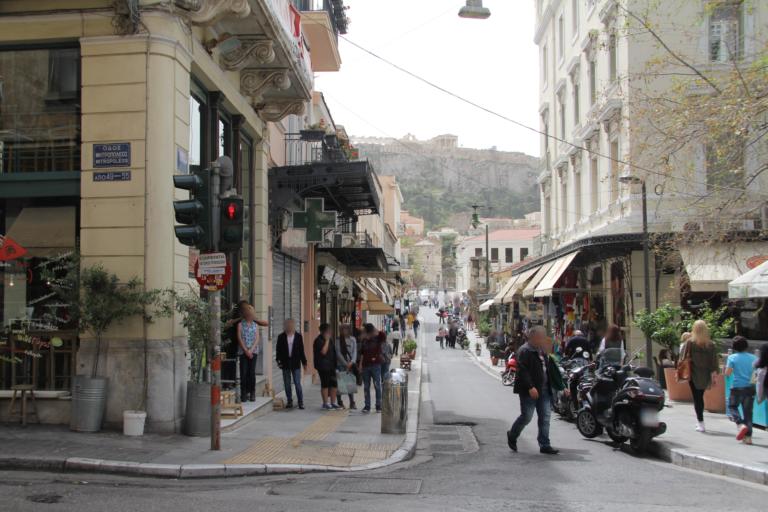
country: GR
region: Attica
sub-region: Nomarchia Athinas
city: Athens
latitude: 37.9761
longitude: 23.7275
